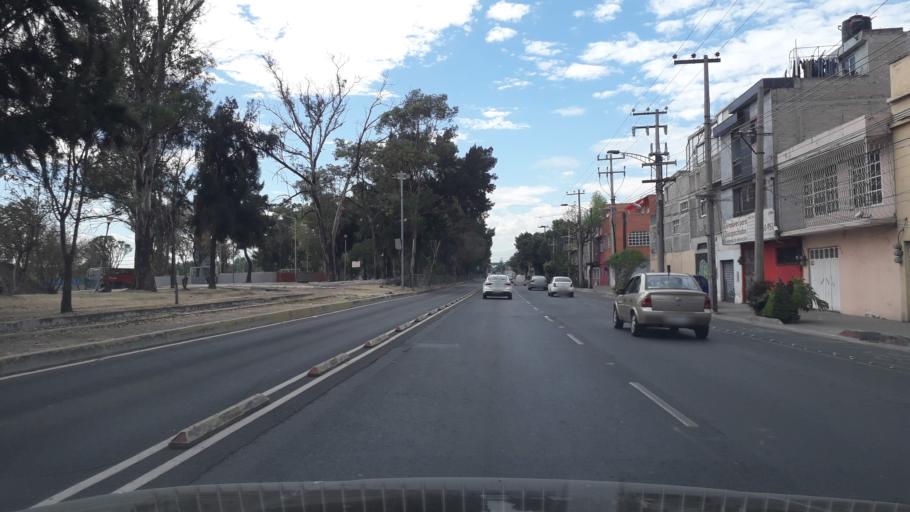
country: MX
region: Mexico City
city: Gustavo A. Madero
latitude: 19.4826
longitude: -99.0967
